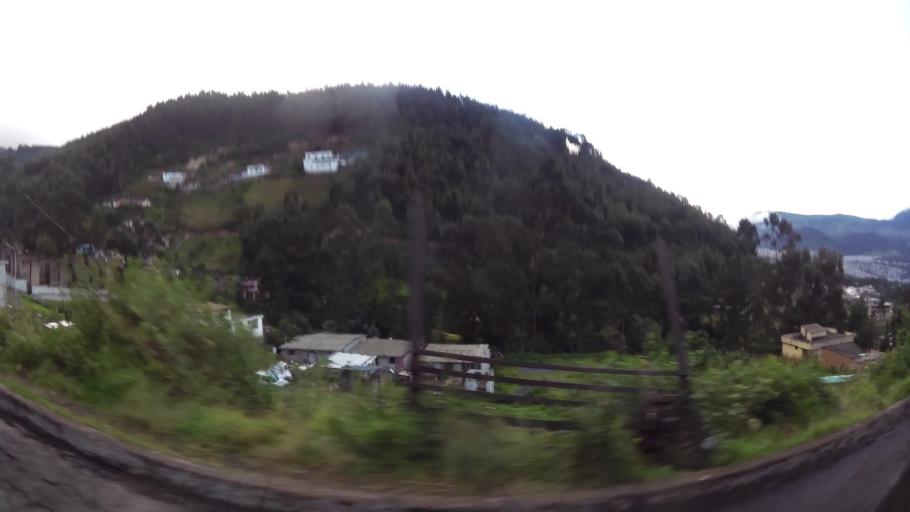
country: EC
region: Pichincha
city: Quito
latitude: -0.1168
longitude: -78.5116
